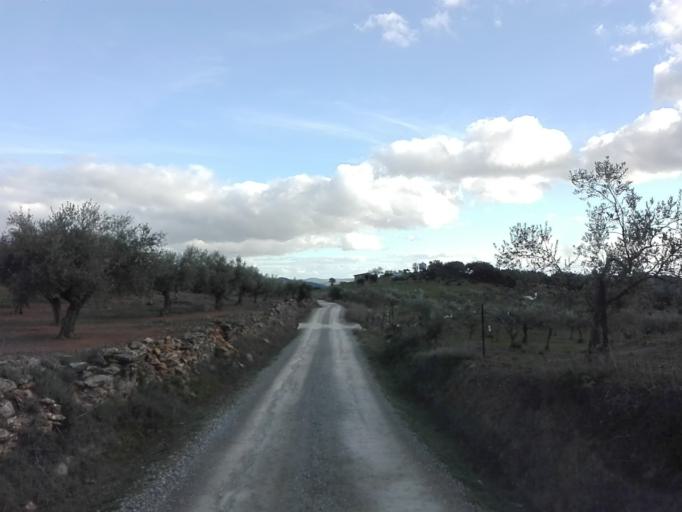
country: ES
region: Extremadura
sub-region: Provincia de Badajoz
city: Trasierra
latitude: 38.1846
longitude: -5.9855
